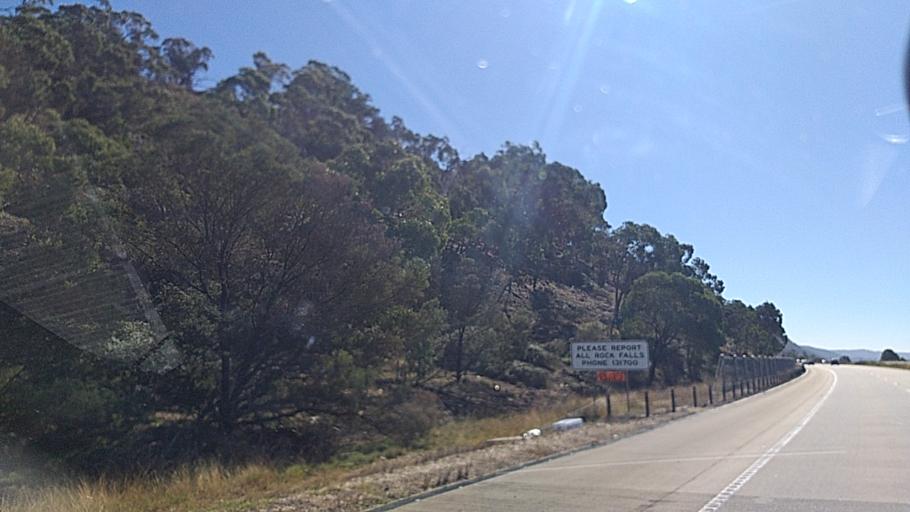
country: AU
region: New South Wales
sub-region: Yass Valley
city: Gundaroo
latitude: -35.0865
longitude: 149.3745
